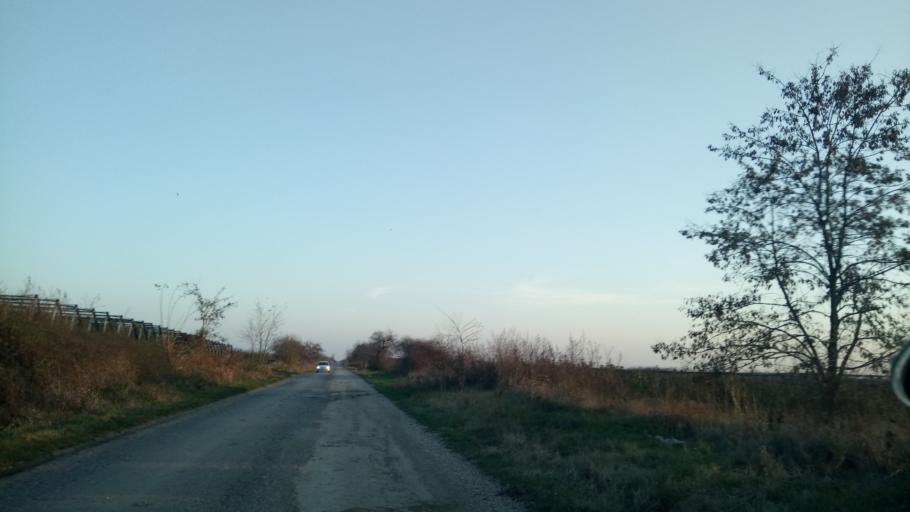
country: RS
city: Novi Slankamen
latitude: 45.1201
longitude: 20.2674
